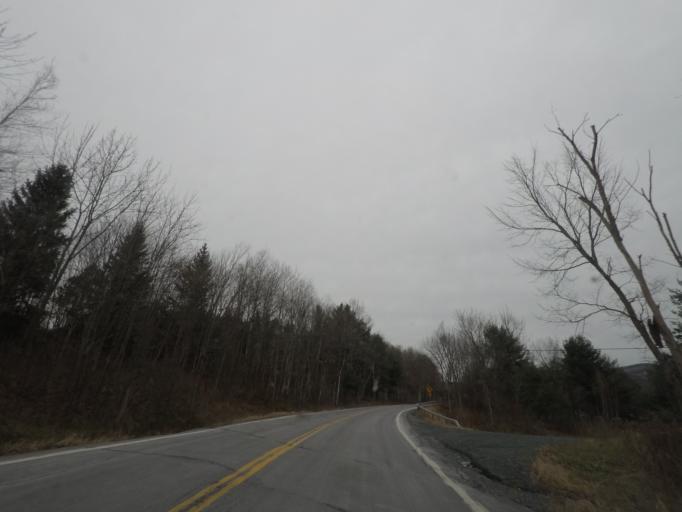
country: US
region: Massachusetts
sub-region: Berkshire County
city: Williamstown
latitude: 42.7445
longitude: -73.3098
